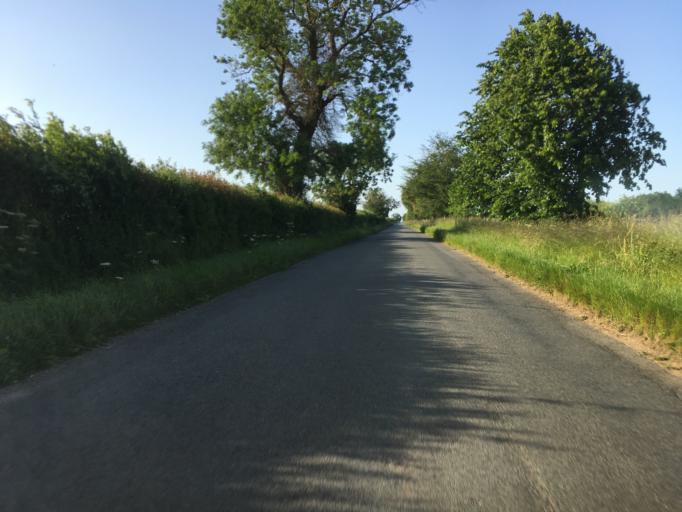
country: GB
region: England
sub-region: Gloucestershire
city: Fairford
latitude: 51.7136
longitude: -1.7679
